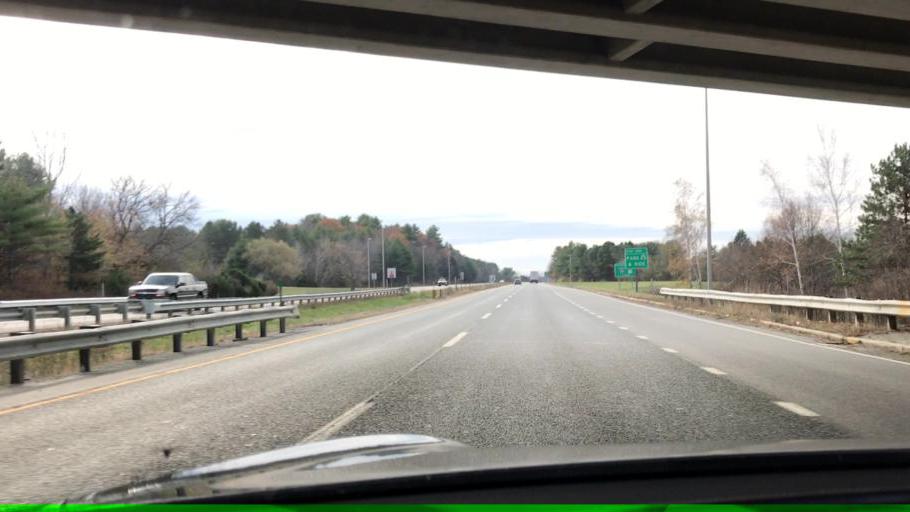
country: US
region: Maine
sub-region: Penobscot County
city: Bangor
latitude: 44.7986
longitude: -68.8021
